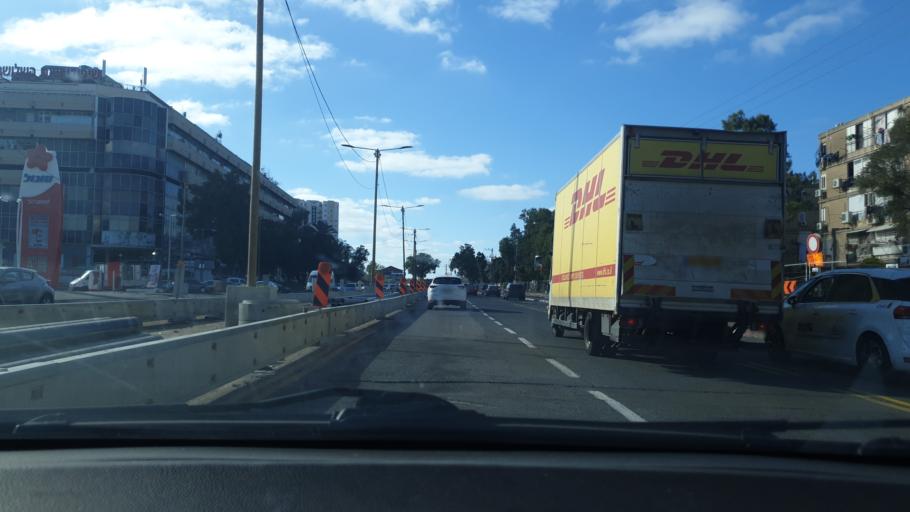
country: IL
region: Tel Aviv
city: Yafo
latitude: 32.0411
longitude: 34.7741
